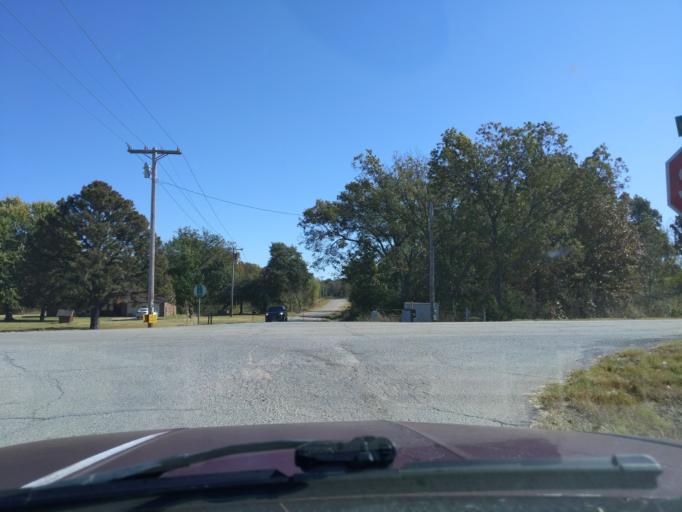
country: US
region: Oklahoma
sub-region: Creek County
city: Bristow
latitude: 35.7119
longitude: -96.3874
